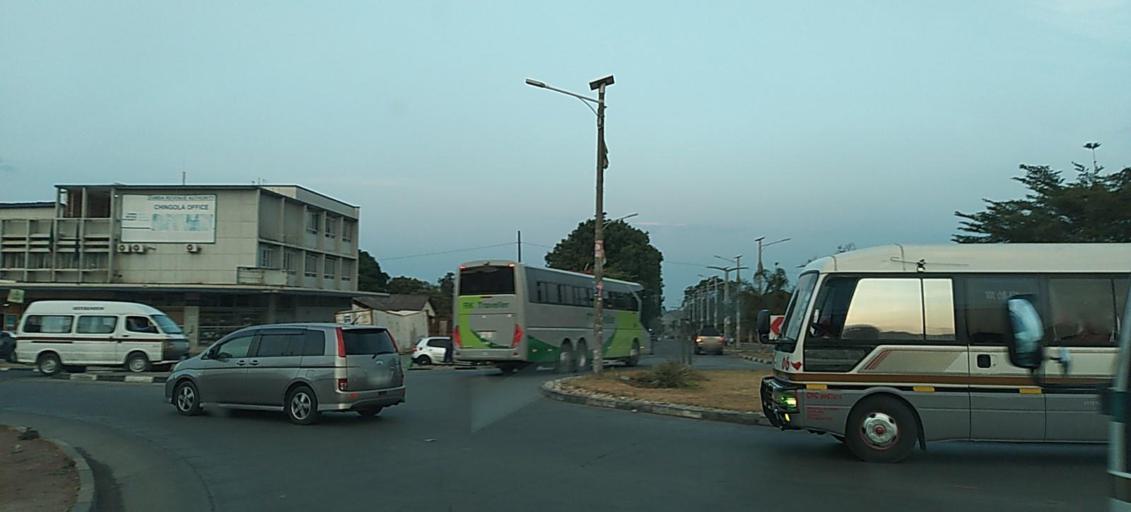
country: ZM
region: Copperbelt
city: Chingola
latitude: -12.5450
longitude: 27.8662
